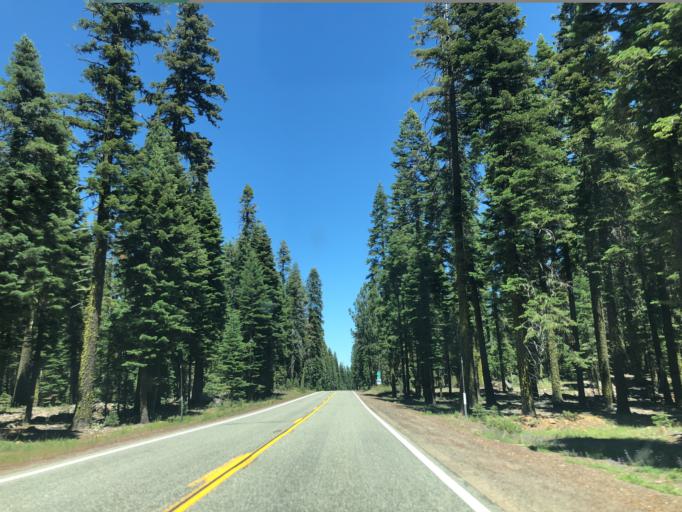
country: US
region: California
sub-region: Shasta County
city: Burney
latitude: 40.5860
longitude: -121.5511
